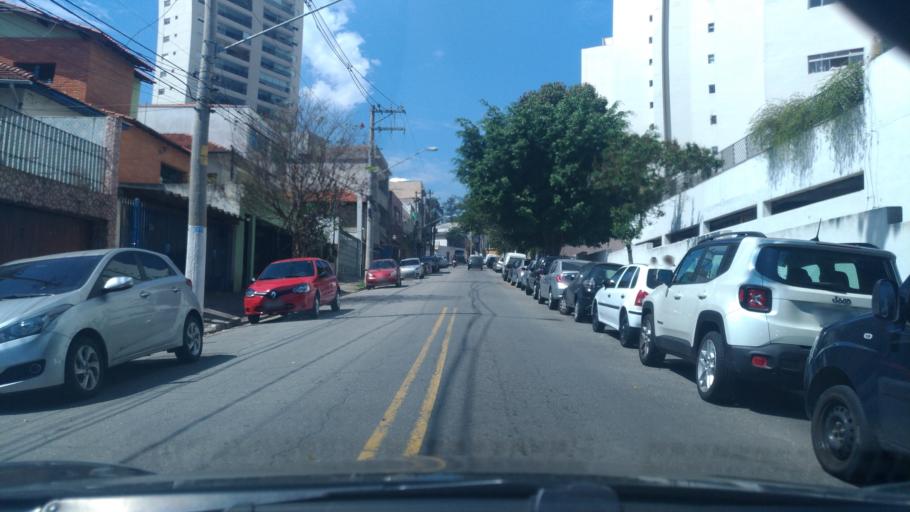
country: BR
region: Sao Paulo
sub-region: Sao Paulo
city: Sao Paulo
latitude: -23.5692
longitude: -46.5920
